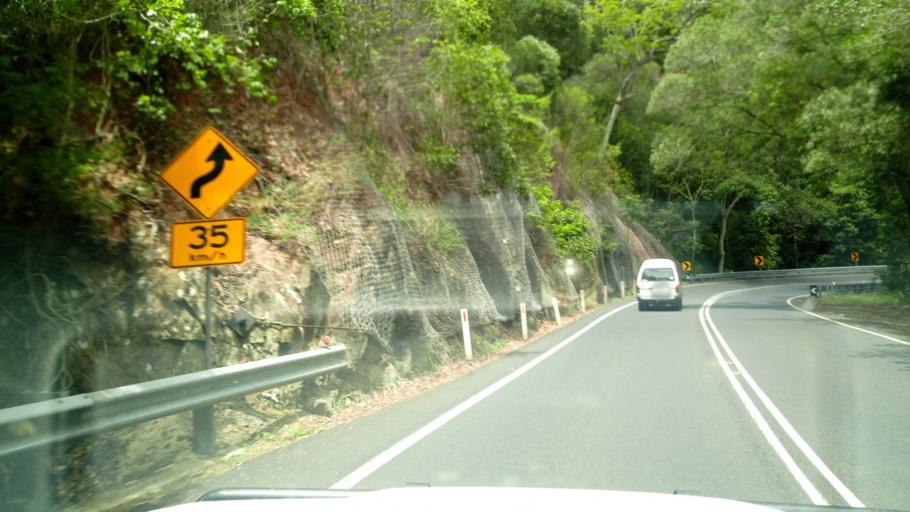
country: AU
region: Queensland
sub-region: Cairns
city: Redlynch
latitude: -16.8417
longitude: 145.6800
